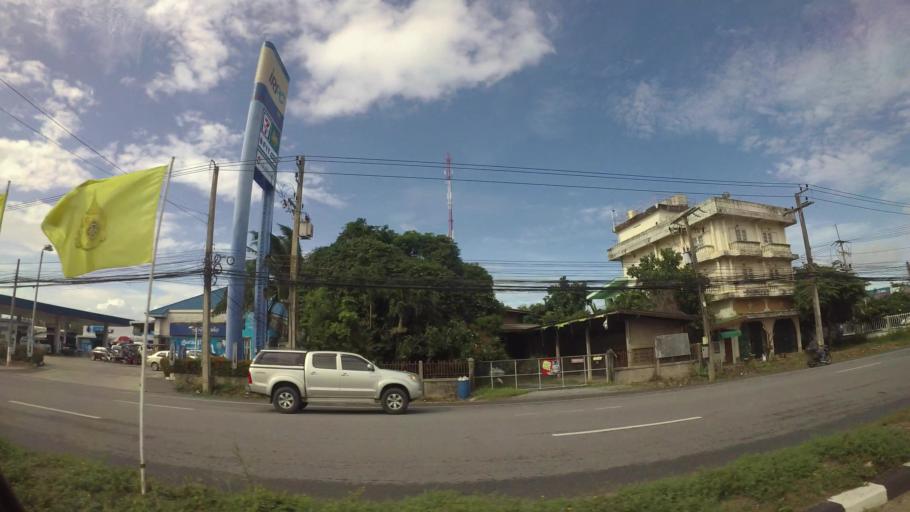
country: TH
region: Rayong
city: Rayong
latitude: 12.6647
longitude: 101.3008
